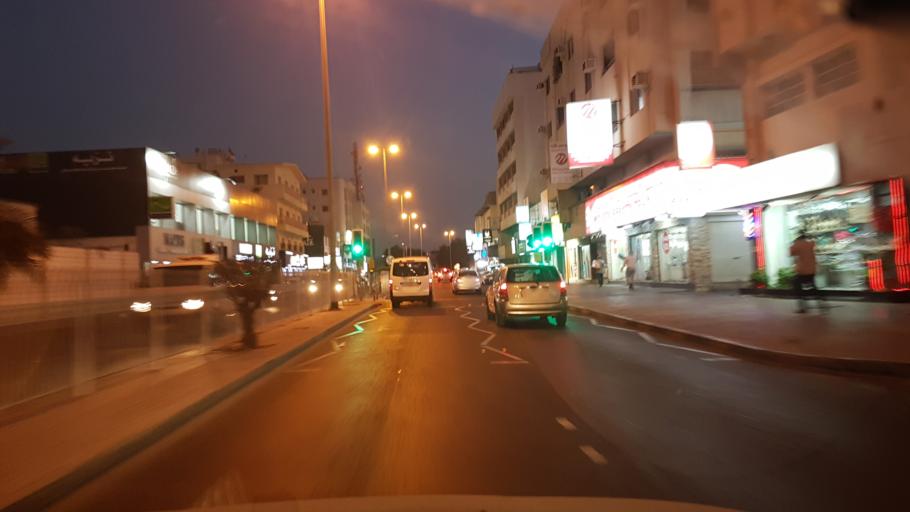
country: BH
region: Manama
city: Manama
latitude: 26.2342
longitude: 50.5885
